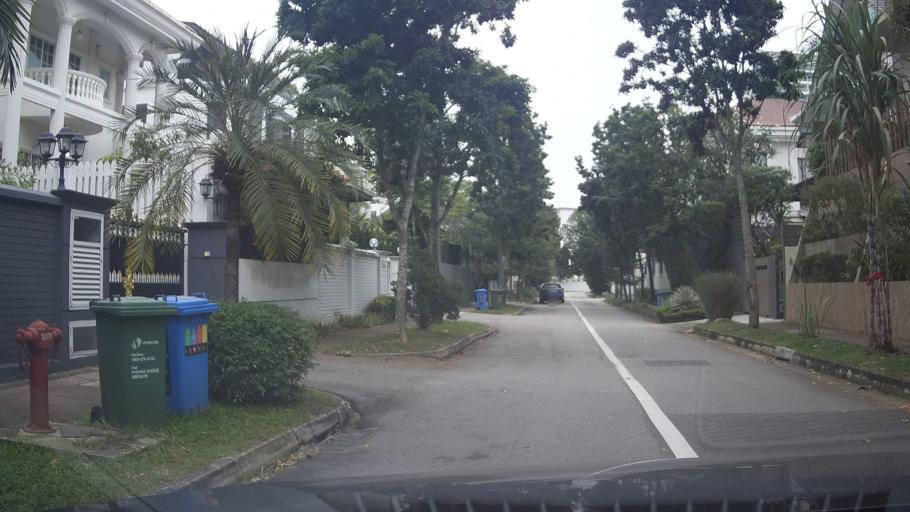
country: SG
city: Singapore
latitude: 1.3041
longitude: 103.8861
